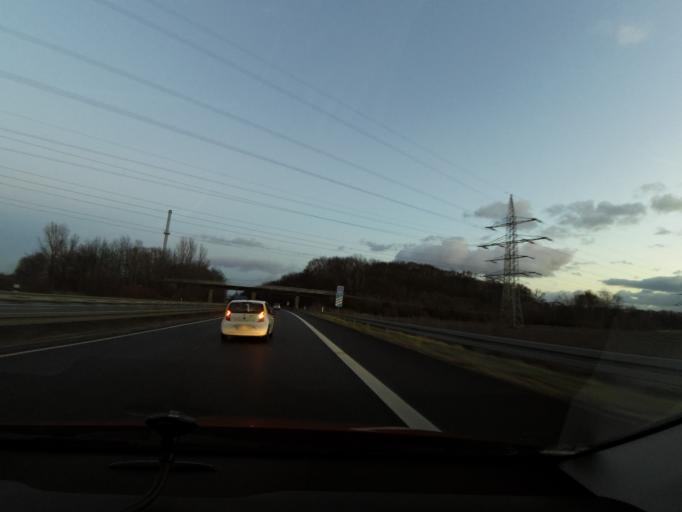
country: DE
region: Lower Saxony
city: Braunschweig
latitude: 52.2895
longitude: 10.4817
